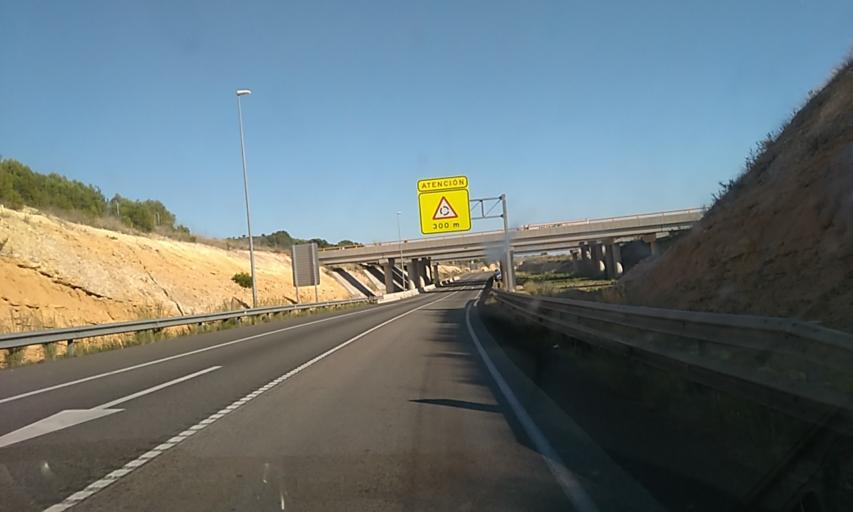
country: ES
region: Valencia
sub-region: Provincia de Castello
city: Torreblanca
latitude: 40.2315
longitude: 0.2079
